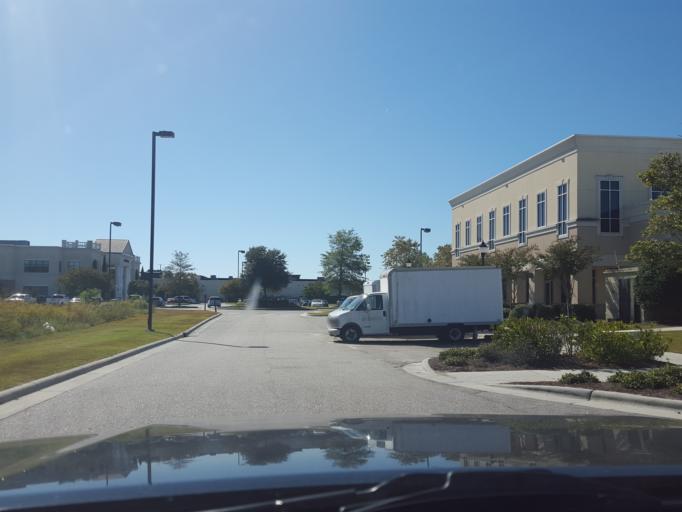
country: US
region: North Carolina
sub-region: New Hanover County
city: Ogden
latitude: 34.2393
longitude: -77.8267
